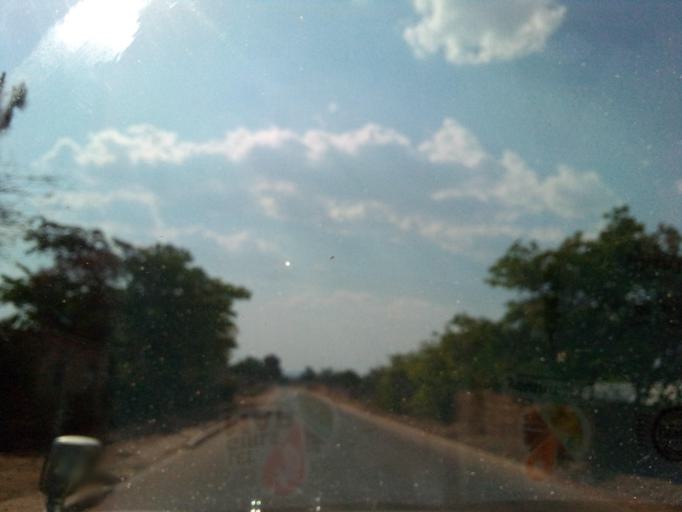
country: ZM
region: Northern
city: Mpika
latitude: -11.8475
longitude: 31.4501
